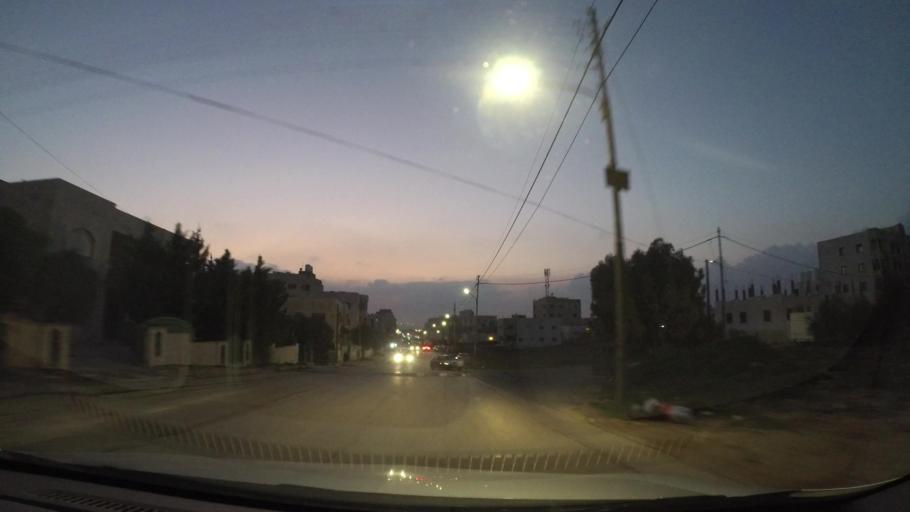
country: JO
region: Amman
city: Al Bunayyat ash Shamaliyah
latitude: 31.8945
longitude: 35.9225
